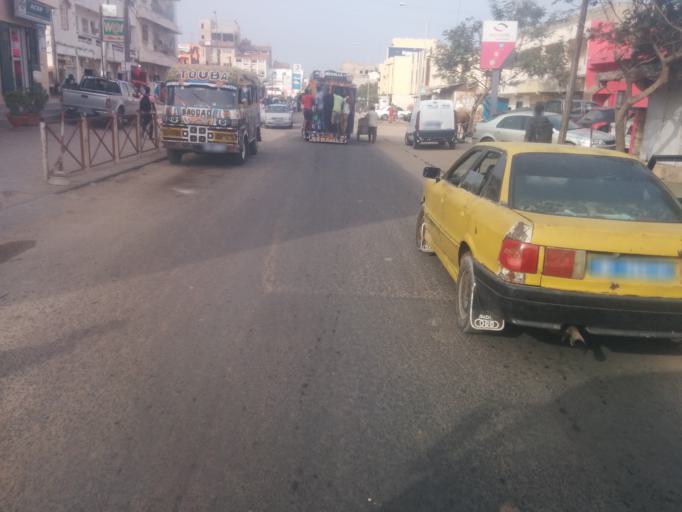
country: SN
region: Dakar
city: Grand Dakar
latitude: 14.7597
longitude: -17.4441
